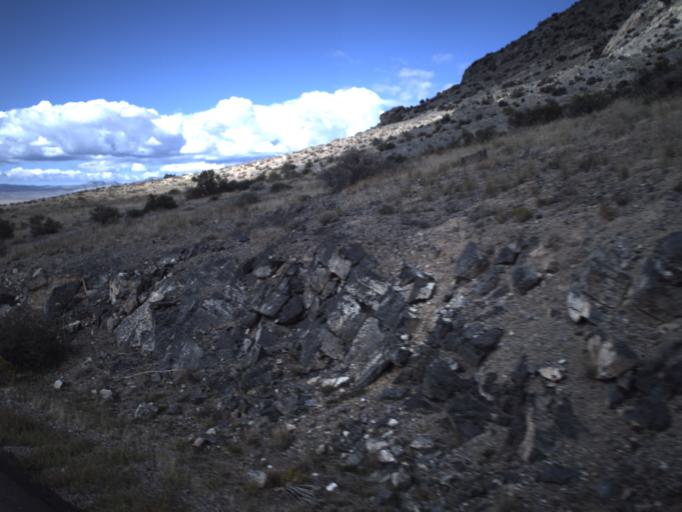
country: US
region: Utah
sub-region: Beaver County
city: Milford
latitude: 38.5084
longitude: -113.5889
